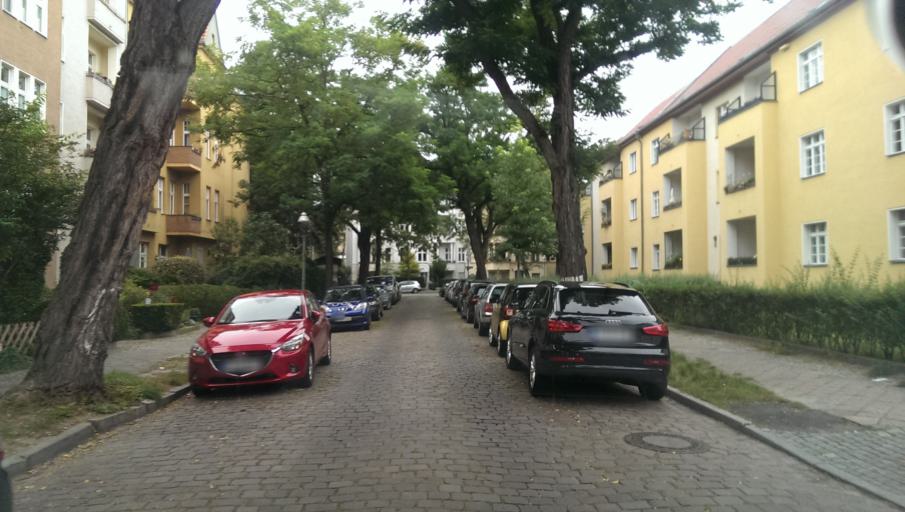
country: DE
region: Berlin
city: Lichterfelde
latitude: 52.4467
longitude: 13.3168
